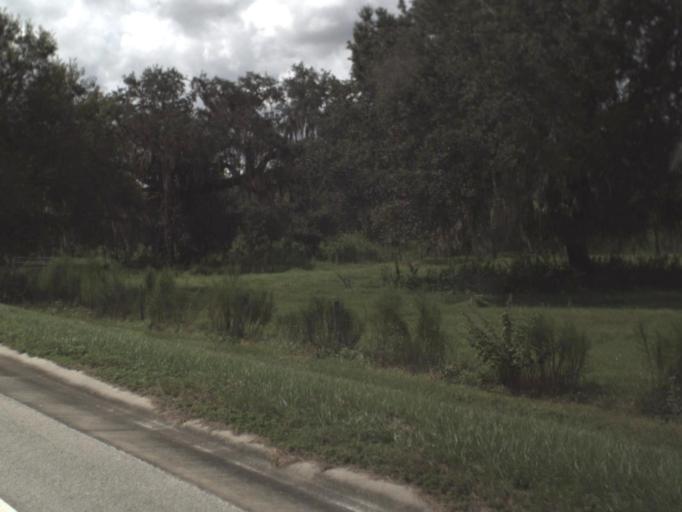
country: US
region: Florida
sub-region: DeSoto County
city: Nocatee
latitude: 27.1998
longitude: -81.9854
